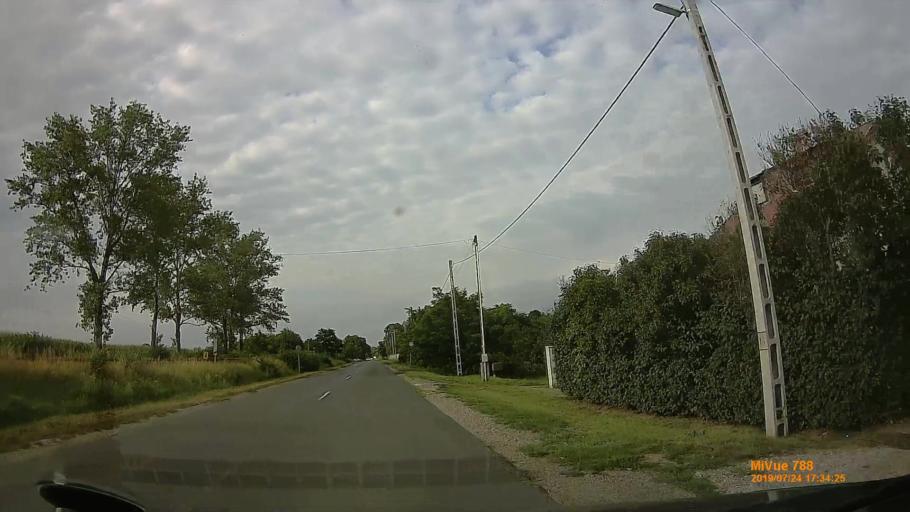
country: HU
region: Borsod-Abauj-Zemplen
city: Abaujszanto
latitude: 48.3041
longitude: 21.1976
